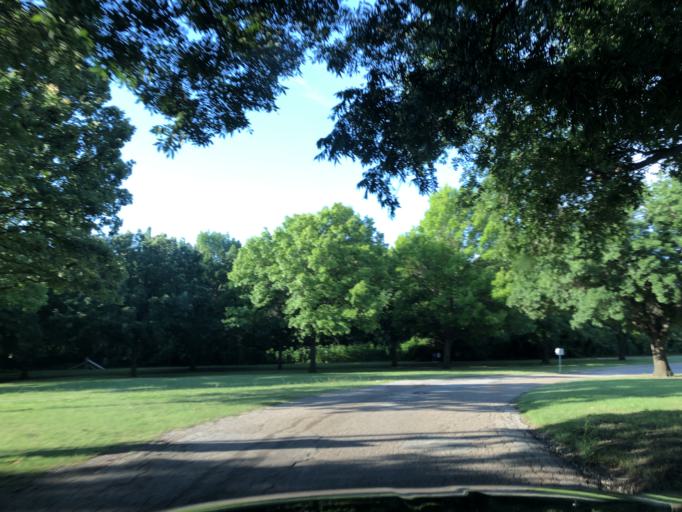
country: US
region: Texas
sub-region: Dallas County
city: Garland
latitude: 32.8473
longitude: -96.6140
